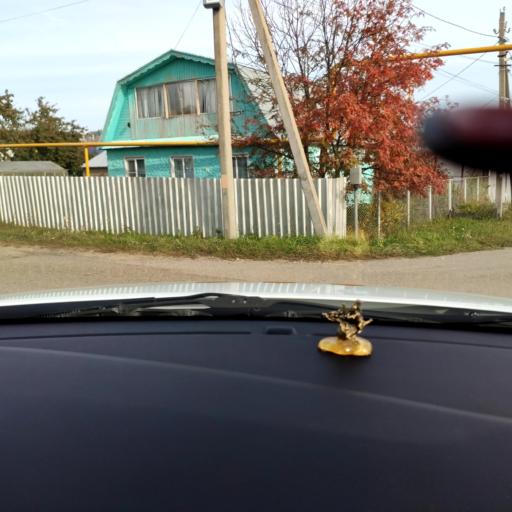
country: RU
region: Tatarstan
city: Vysokaya Gora
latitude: 55.9141
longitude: 49.2959
